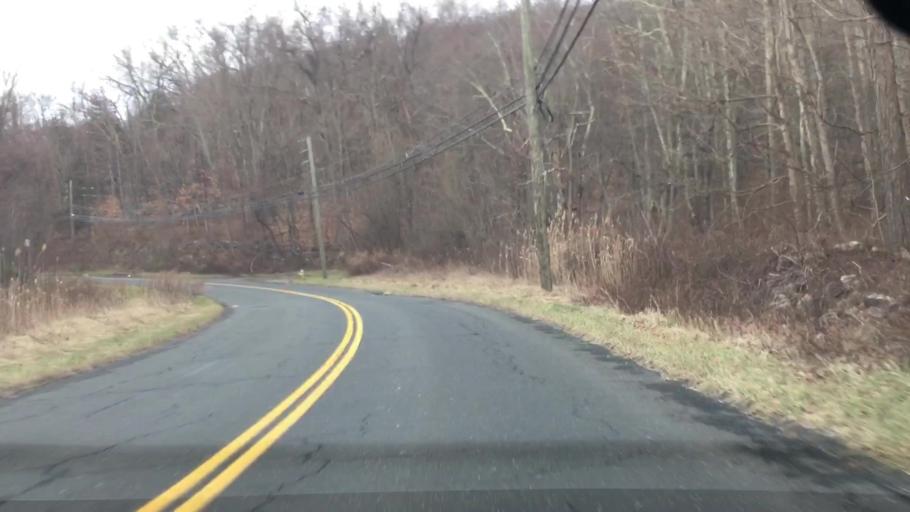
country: US
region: New York
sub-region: Putnam County
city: Peach Lake
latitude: 41.3748
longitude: -73.5279
